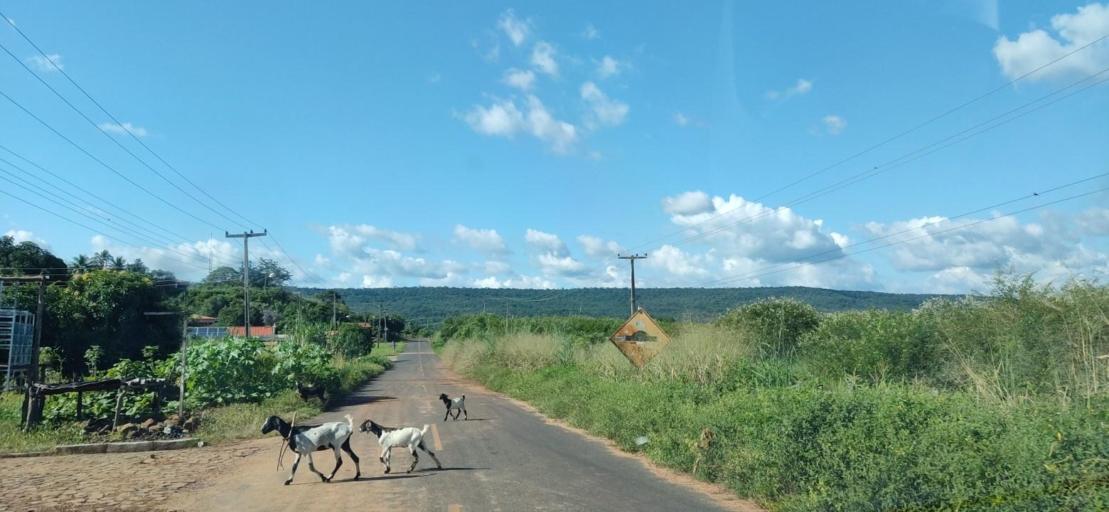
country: BR
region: Piaui
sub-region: Valenca Do Piaui
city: Valenca do Piaui
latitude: -6.1755
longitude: -41.8182
